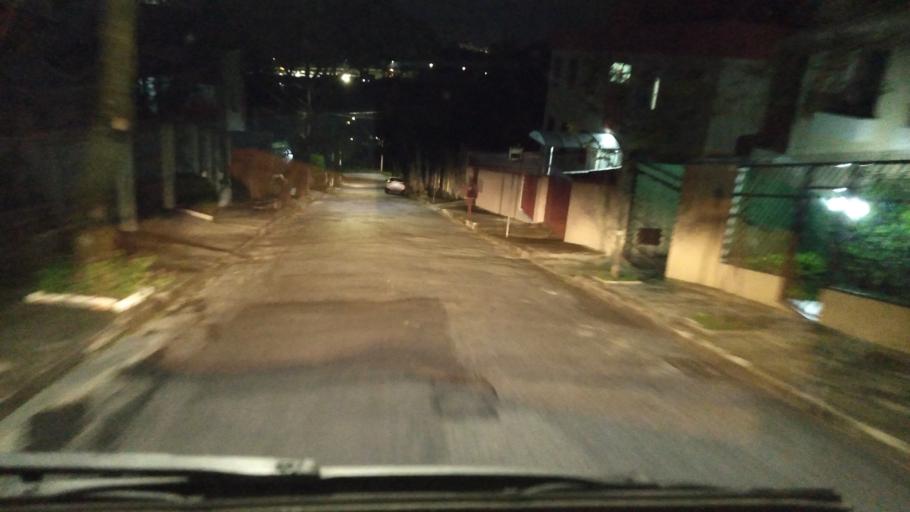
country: BR
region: Minas Gerais
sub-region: Belo Horizonte
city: Belo Horizonte
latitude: -19.8967
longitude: -43.9733
